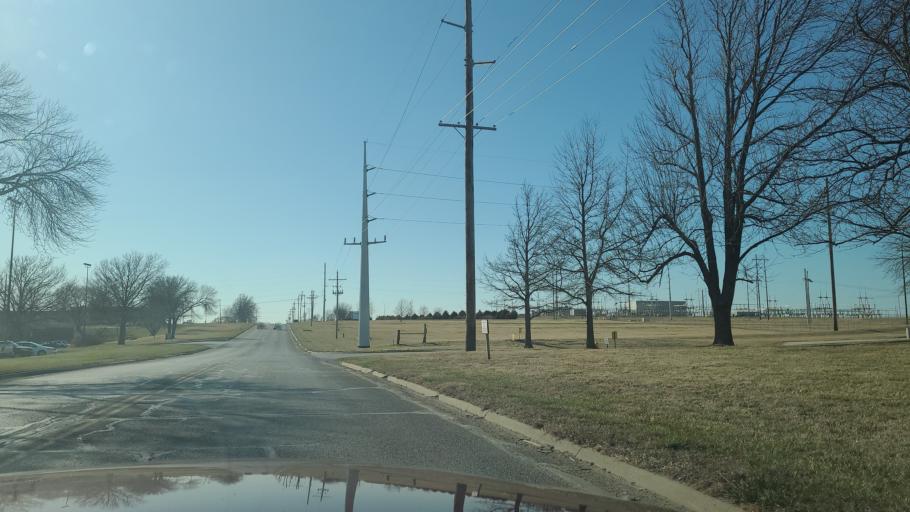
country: US
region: Kansas
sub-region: Douglas County
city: Lawrence
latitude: 39.0007
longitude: -95.2667
